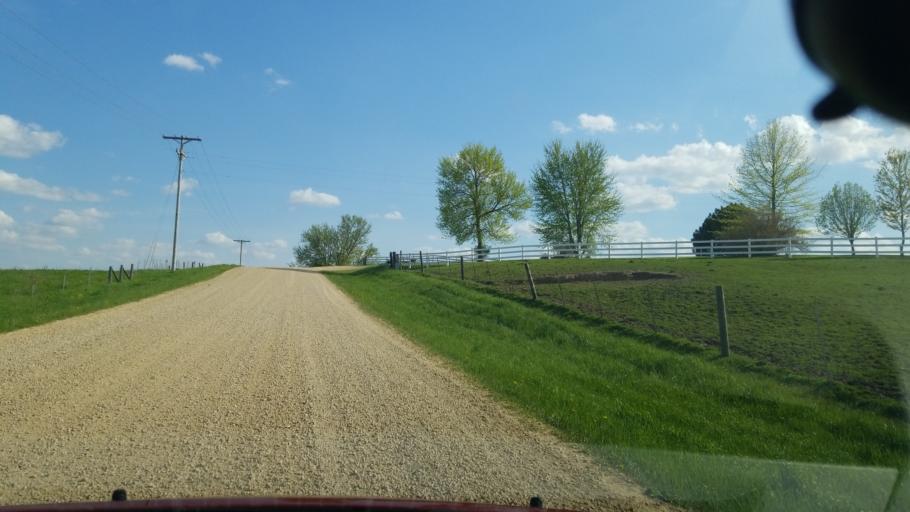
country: US
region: Iowa
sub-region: Jackson County
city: Maquoketa
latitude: 42.2033
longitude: -90.7294
